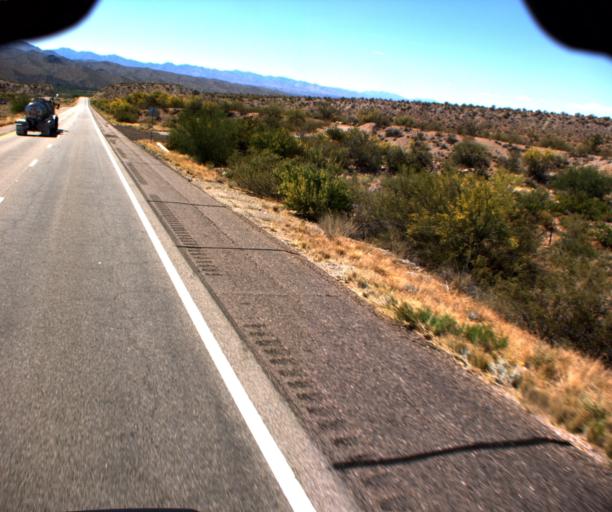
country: US
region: Arizona
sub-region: Yavapai County
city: Bagdad
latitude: 34.6313
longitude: -113.5455
